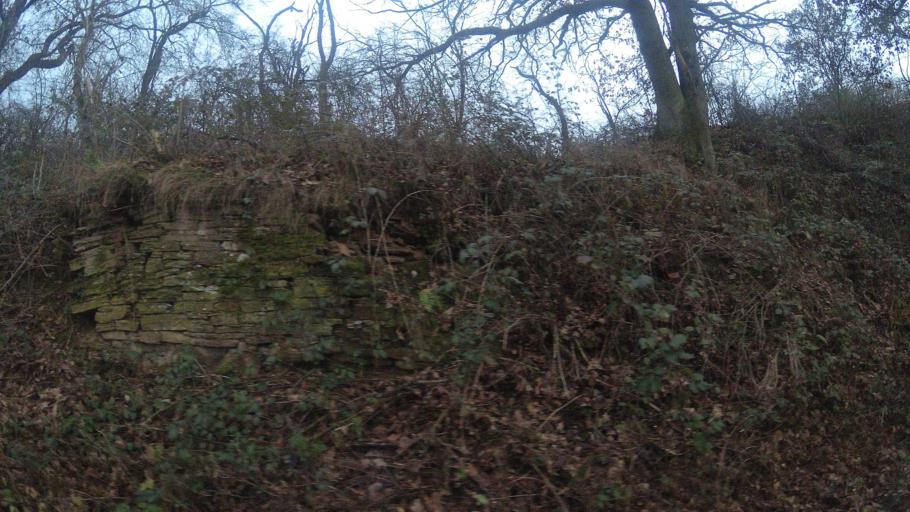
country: DE
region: Rheinland-Pfalz
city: Offenbach-Hundheim
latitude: 49.6133
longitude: 7.5353
